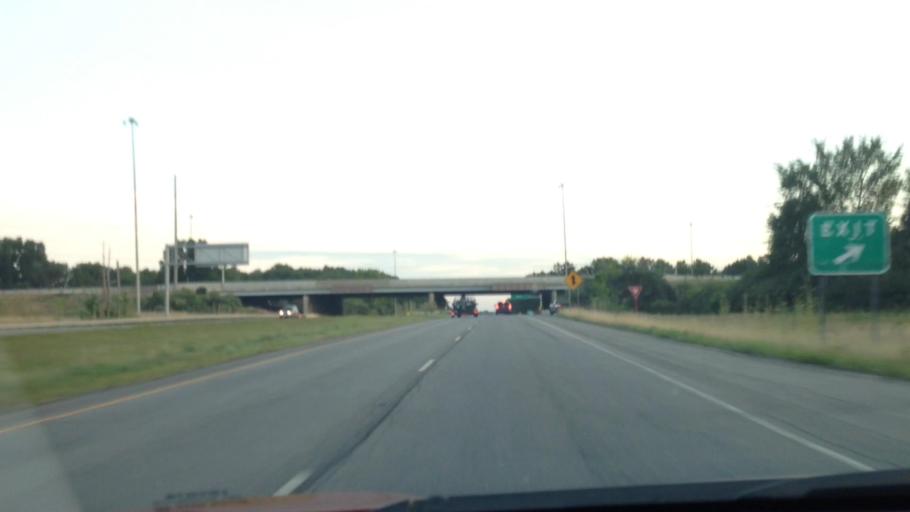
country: US
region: Ohio
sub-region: Summit County
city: Norton
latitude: 41.0418
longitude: -81.6628
